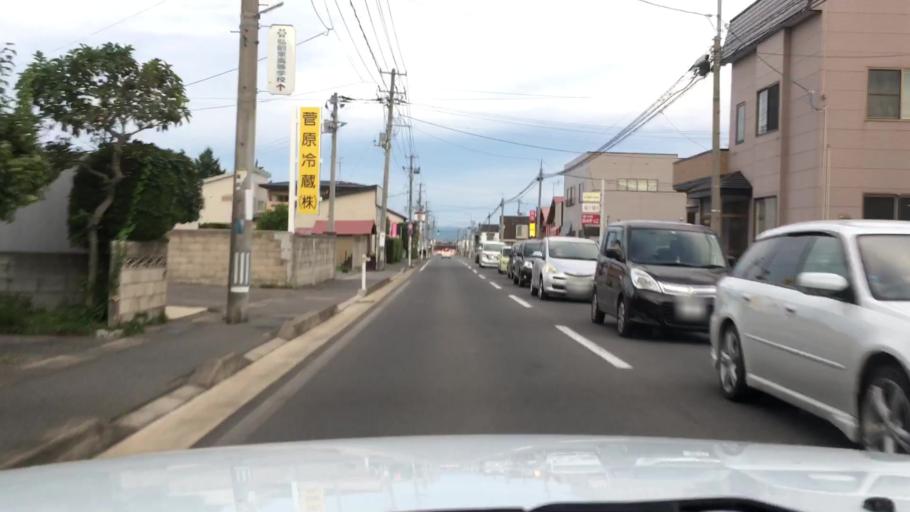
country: JP
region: Aomori
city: Hirosaki
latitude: 40.5902
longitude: 140.4840
